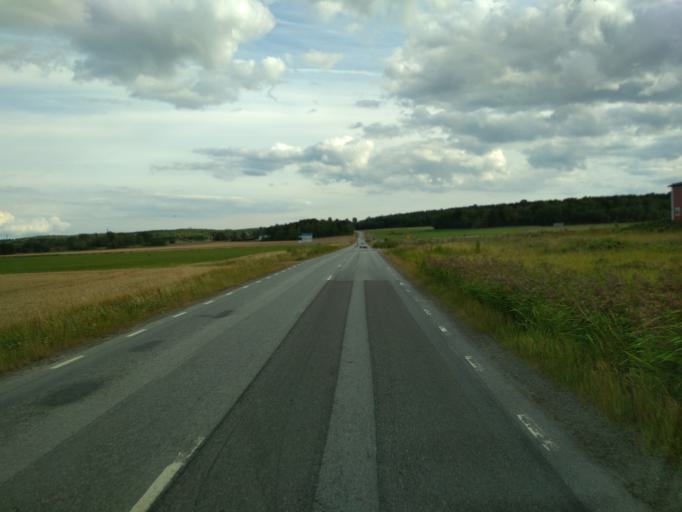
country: SE
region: Uppsala
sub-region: Habo Kommun
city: Balsta
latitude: 59.6634
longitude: 17.5548
